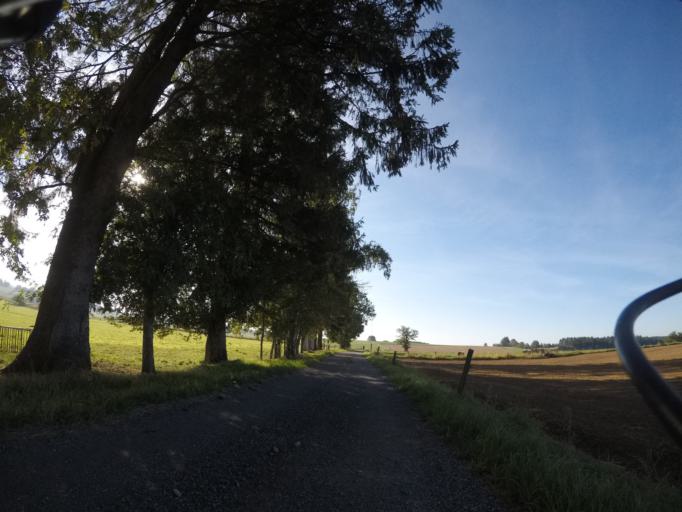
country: BE
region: Wallonia
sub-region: Province du Luxembourg
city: Fauvillers
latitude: 49.9187
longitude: 5.6577
